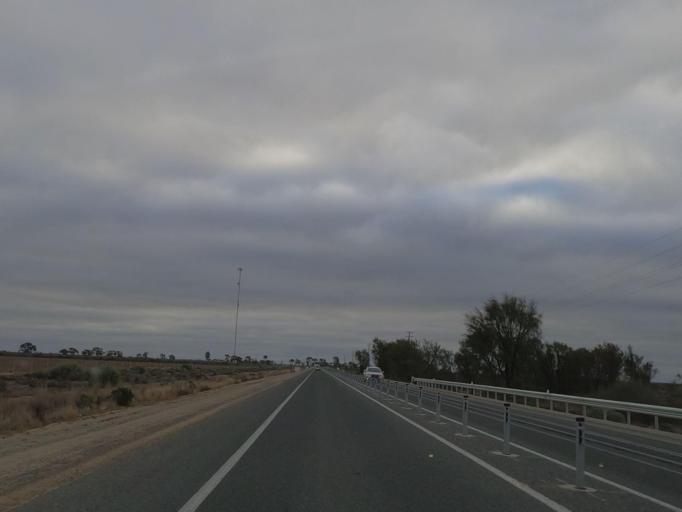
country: AU
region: Victoria
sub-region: Swan Hill
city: Swan Hill
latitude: -35.5312
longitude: 143.7405
